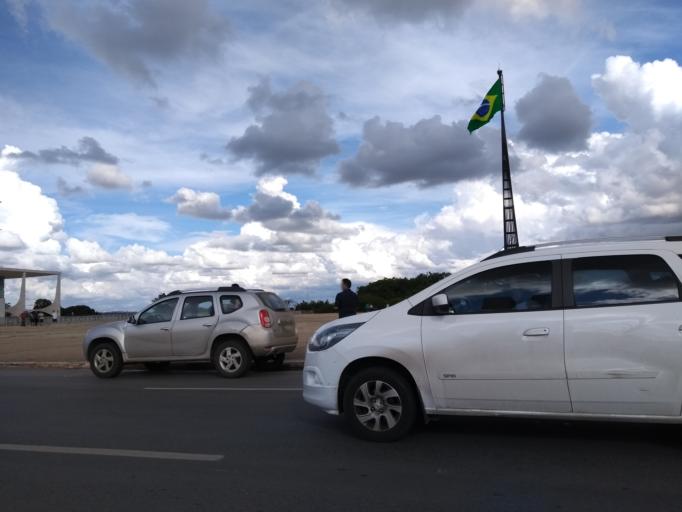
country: BR
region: Federal District
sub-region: Brasilia
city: Brasilia
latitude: -15.8002
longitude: -47.8618
